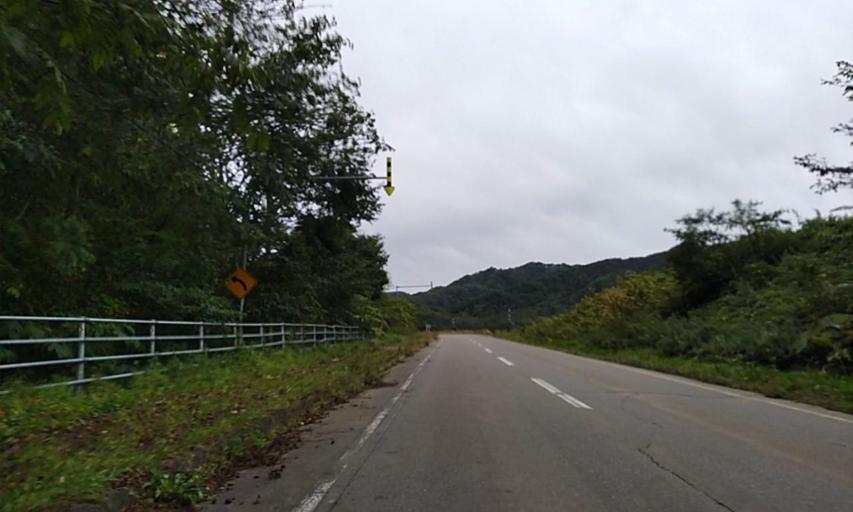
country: JP
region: Hokkaido
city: Obihiro
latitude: 42.6912
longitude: 143.0534
